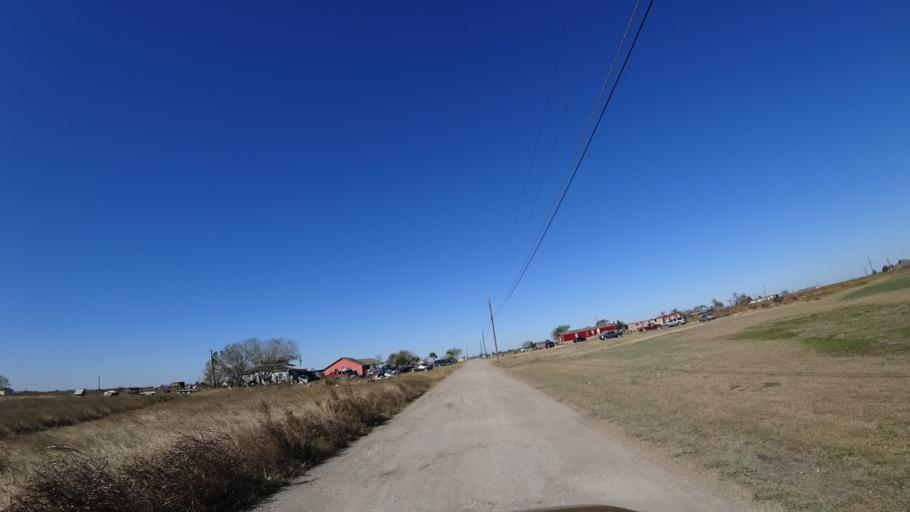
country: US
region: Texas
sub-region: Travis County
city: Garfield
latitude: 30.0990
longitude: -97.6163
